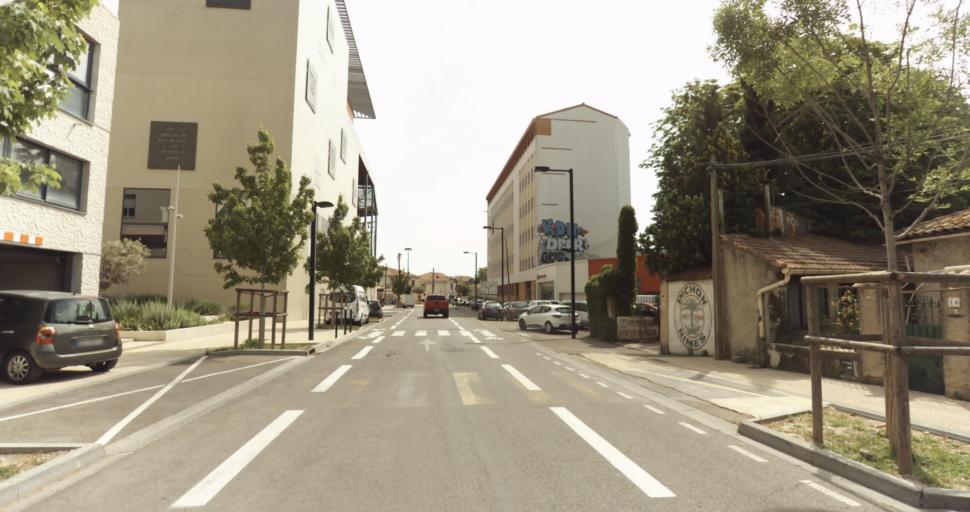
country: FR
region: Languedoc-Roussillon
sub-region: Departement du Gard
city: Nimes
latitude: 43.8308
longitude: 4.3679
